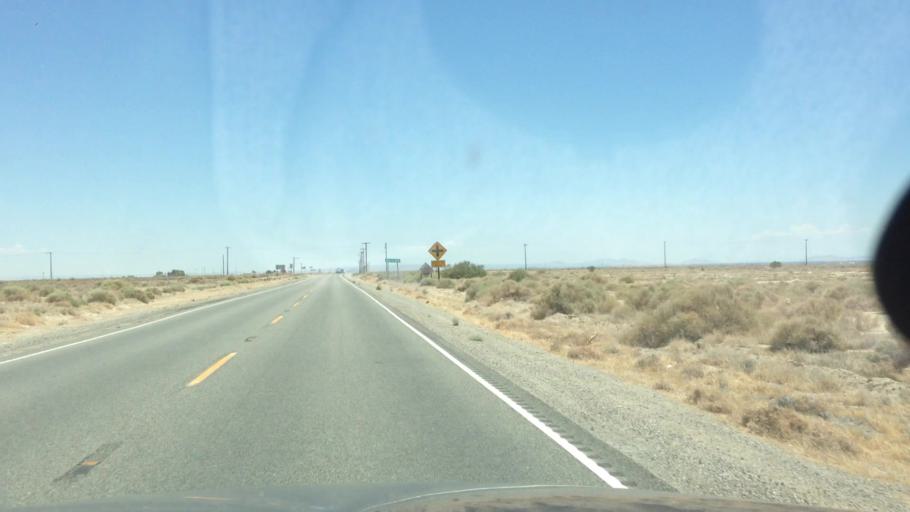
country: US
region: California
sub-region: Kern County
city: Rosamond
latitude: 34.7767
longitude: -118.2418
